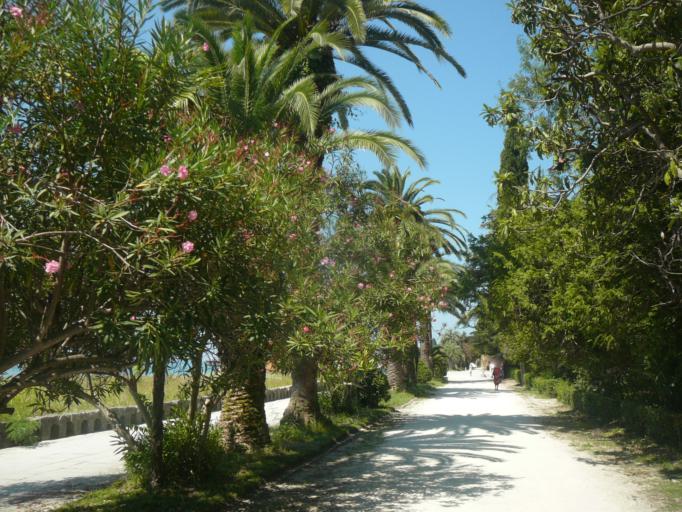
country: GE
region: Abkhazia
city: Gagra
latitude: 43.3230
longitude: 40.2302
